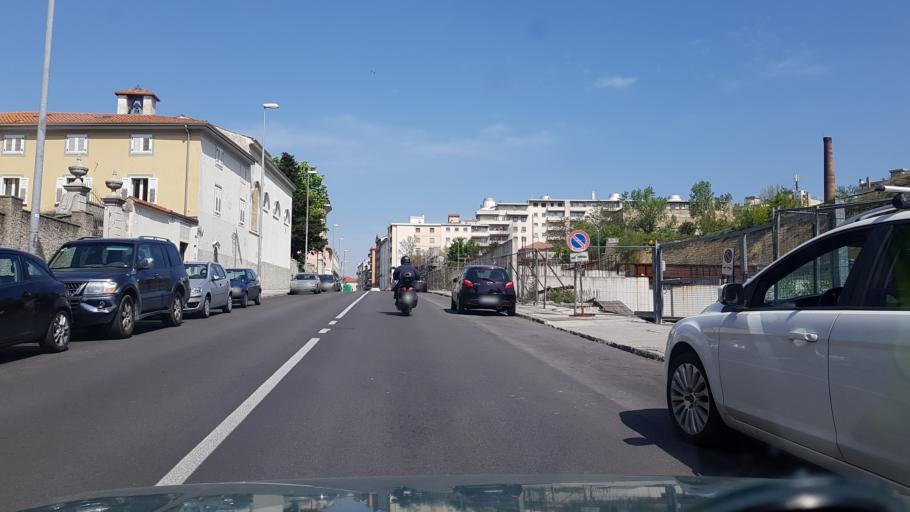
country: IT
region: Friuli Venezia Giulia
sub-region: Provincia di Trieste
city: Trieste
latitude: 45.6362
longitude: 13.7858
